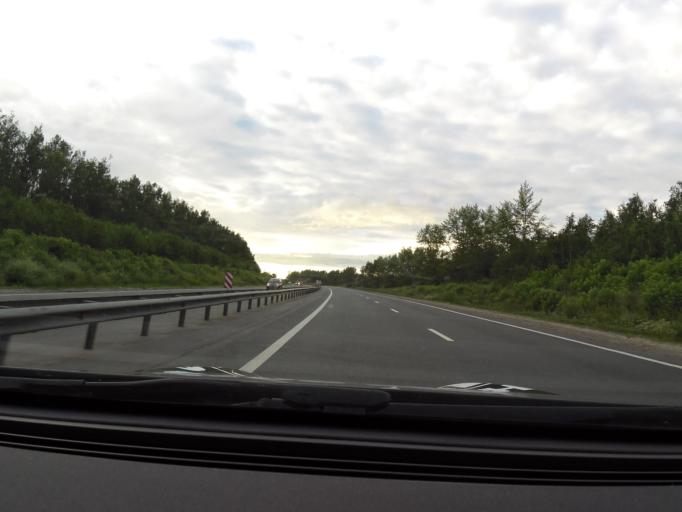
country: RU
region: Chuvashia
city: Kugesi
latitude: 55.9906
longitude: 47.3434
